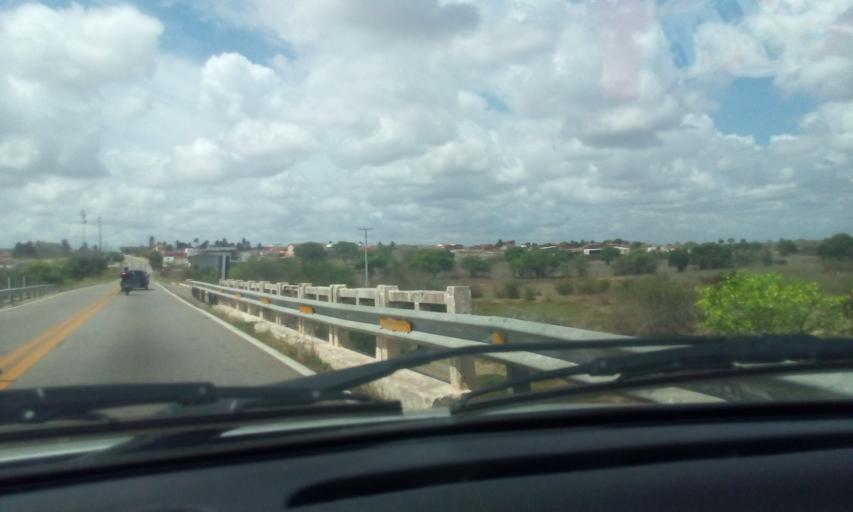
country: BR
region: Rio Grande do Norte
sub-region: Sao Paulo Do Potengi
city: Sao Paulo do Potengi
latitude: -5.9794
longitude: -35.5774
